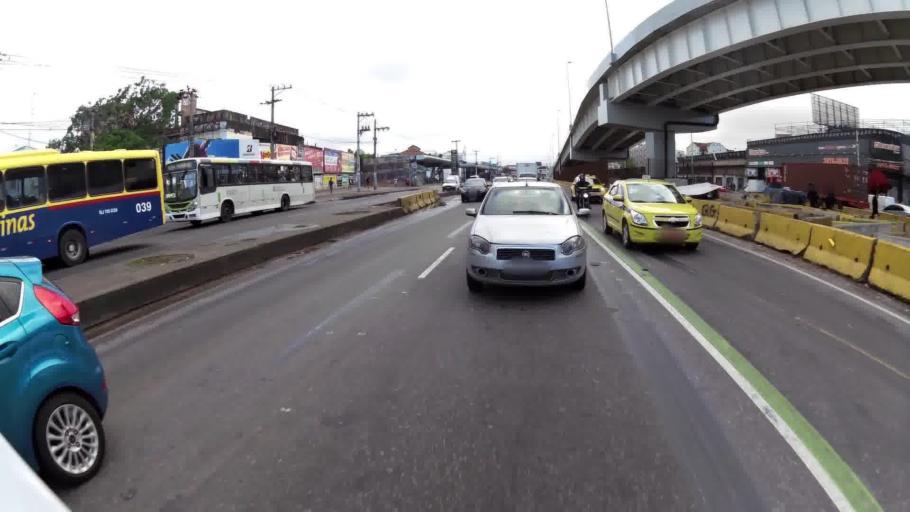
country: BR
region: Rio de Janeiro
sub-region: Rio De Janeiro
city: Rio de Janeiro
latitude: -22.8538
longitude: -43.2476
